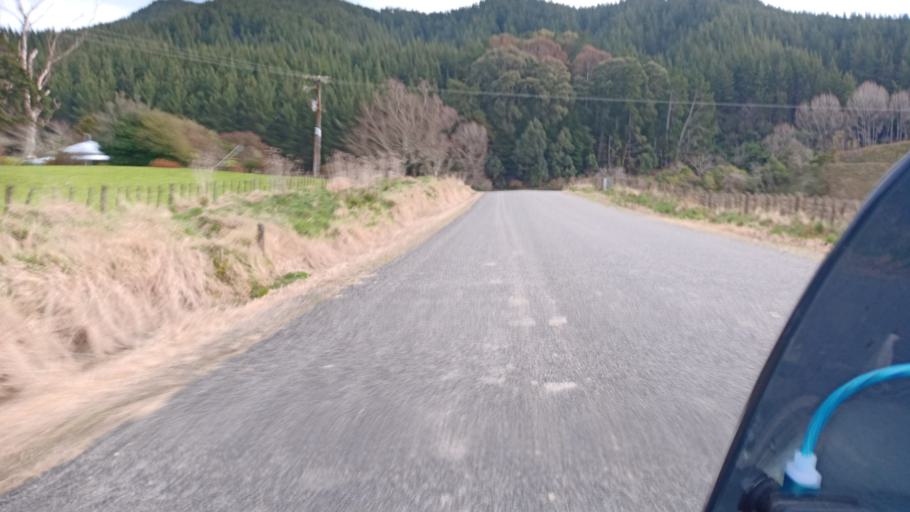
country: NZ
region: Hawke's Bay
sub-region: Wairoa District
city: Wairoa
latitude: -38.8182
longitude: 177.4747
